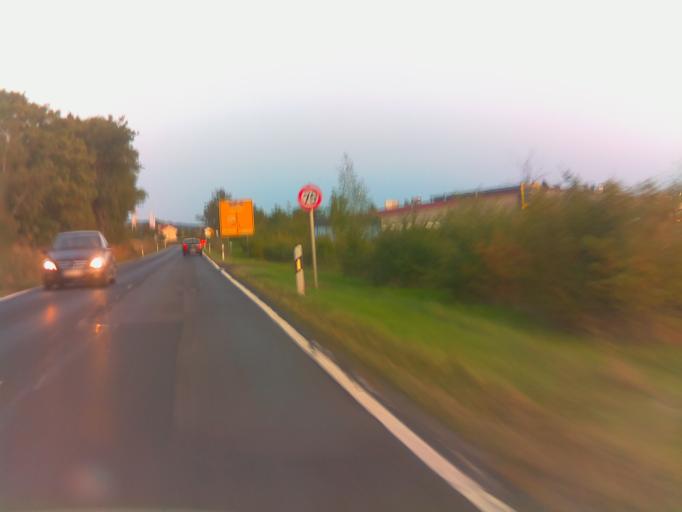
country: DE
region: Bavaria
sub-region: Regierungsbezirk Unterfranken
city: Oerlenbach
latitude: 50.1468
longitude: 10.1286
